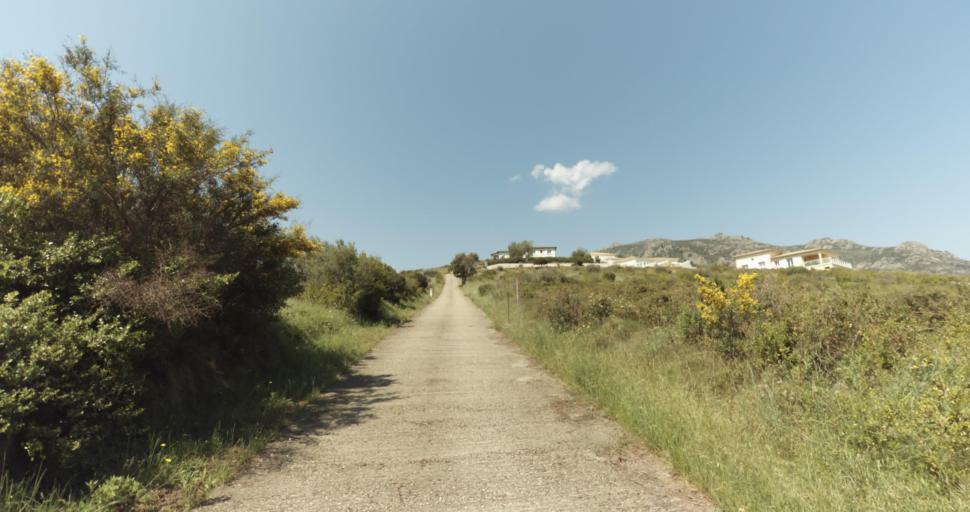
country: FR
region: Corsica
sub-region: Departement de la Haute-Corse
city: Biguglia
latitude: 42.6192
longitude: 9.4316
